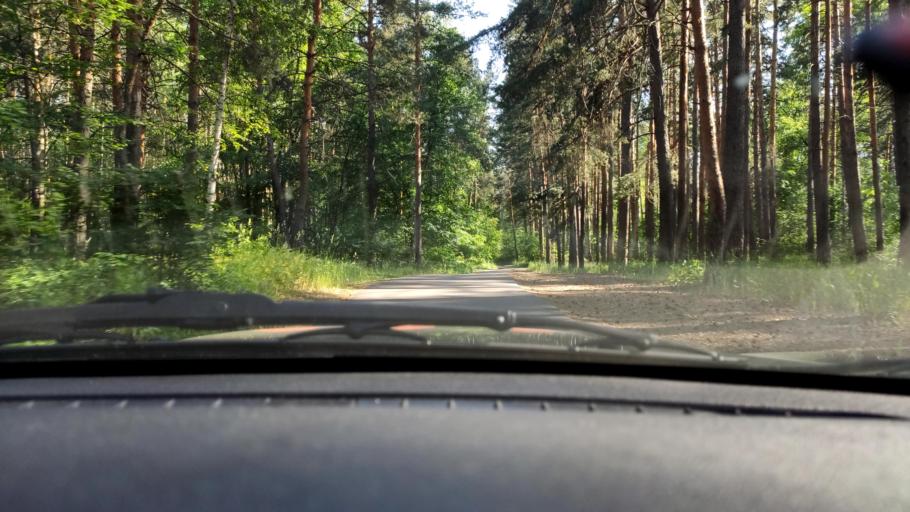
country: RU
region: Voronezj
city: Somovo
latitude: 51.8007
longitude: 39.3803
